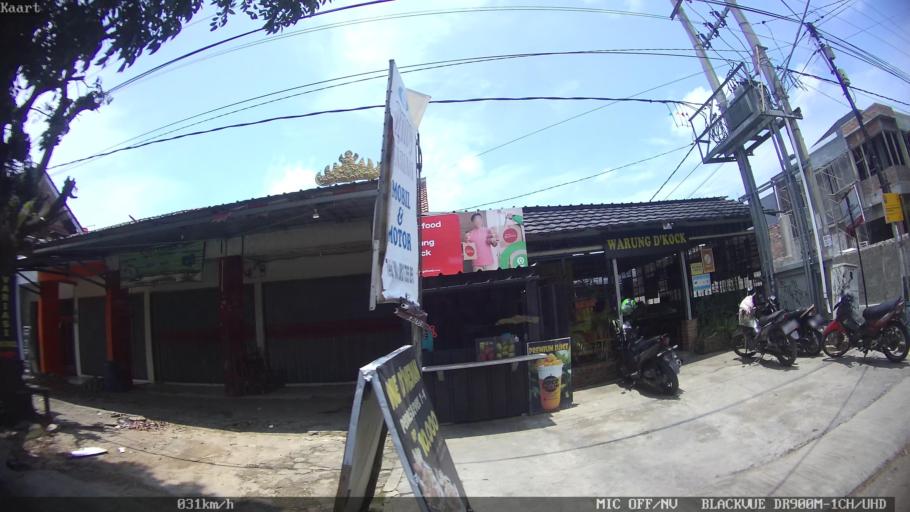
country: ID
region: Lampung
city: Kedaton
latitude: -5.3889
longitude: 105.2493
